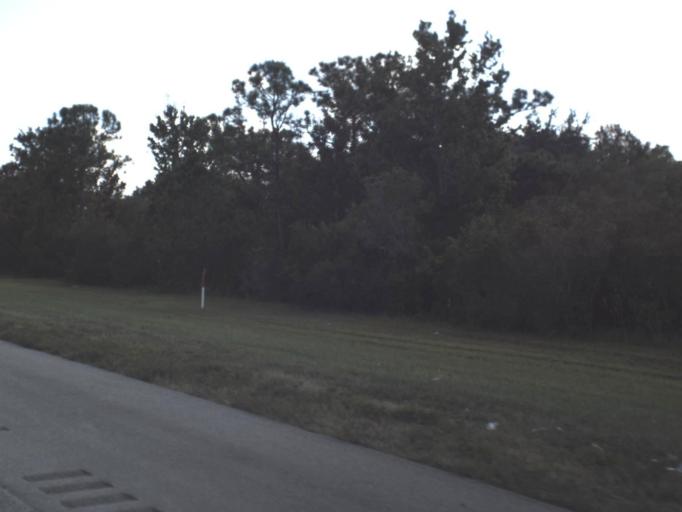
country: US
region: Florida
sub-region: Indian River County
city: Fellsmere
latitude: 27.7359
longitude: -80.9221
